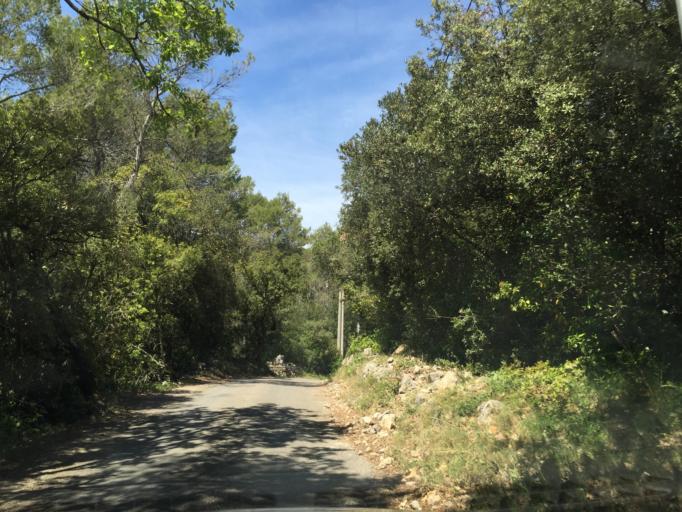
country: FR
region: Provence-Alpes-Cote d'Azur
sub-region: Departement du Var
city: Lorgues
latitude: 43.4761
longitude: 6.3682
